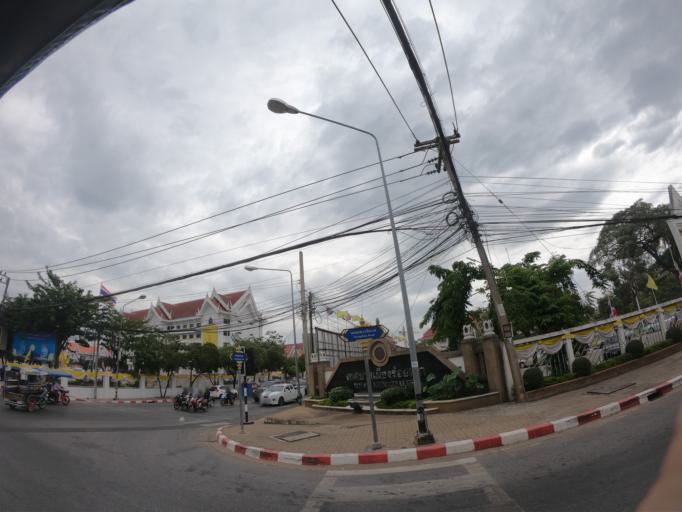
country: TH
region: Roi Et
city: Roi Et
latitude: 16.0540
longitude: 103.6514
